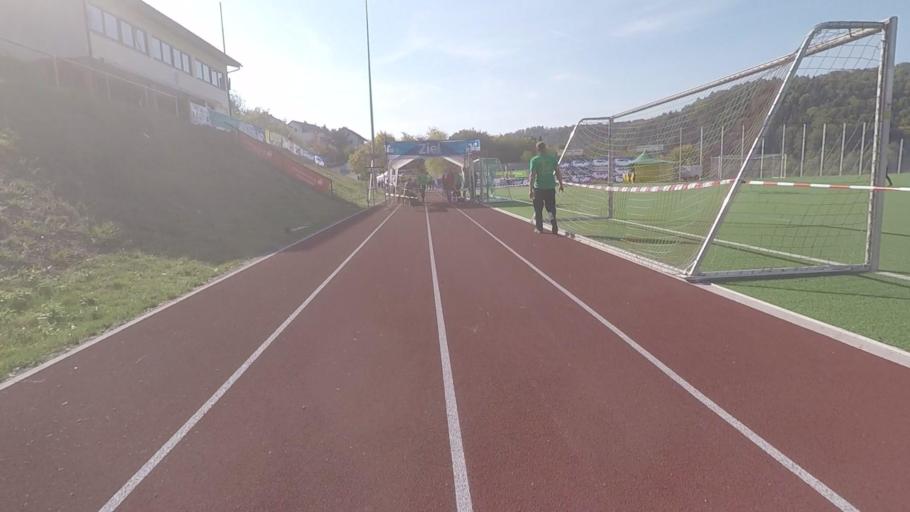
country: DE
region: Baden-Wuerttemberg
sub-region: Regierungsbezirk Stuttgart
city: Spiegelberg
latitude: 49.0377
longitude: 9.4501
